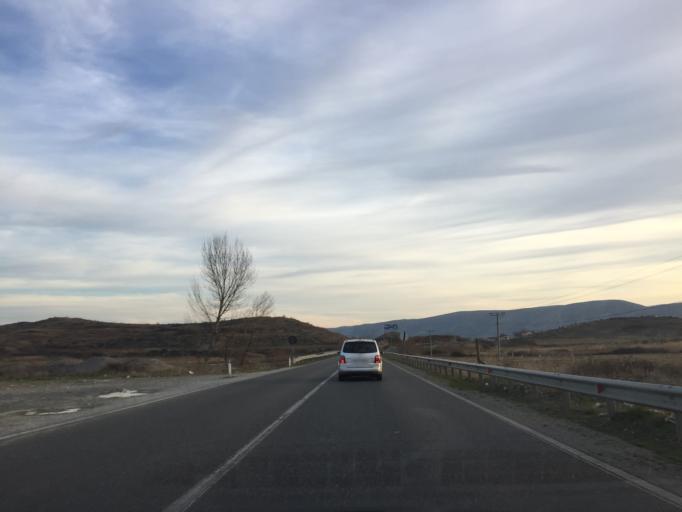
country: AL
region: Shkoder
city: Vukatane
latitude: 41.9616
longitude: 19.5522
